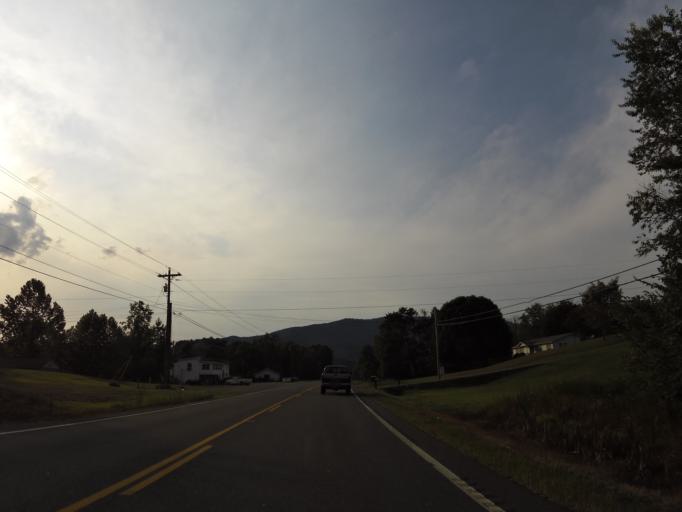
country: US
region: Tennessee
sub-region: Morgan County
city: Coalfield
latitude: 36.0625
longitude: -84.4488
